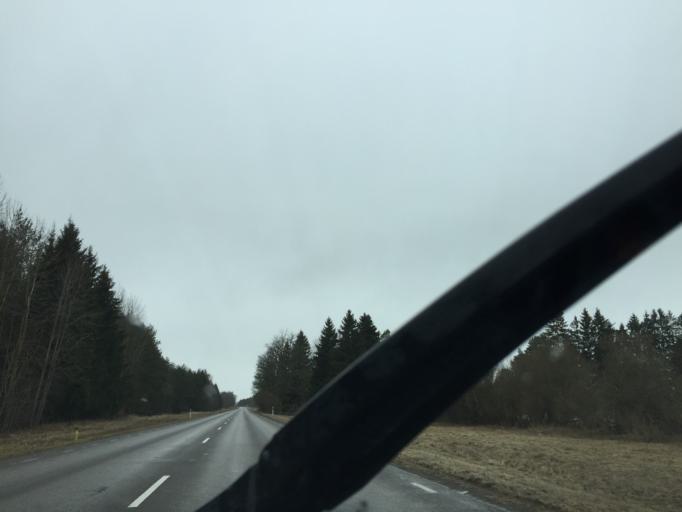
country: EE
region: Laeaene
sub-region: Ridala Parish
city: Uuemoisa
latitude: 58.8731
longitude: 23.6148
